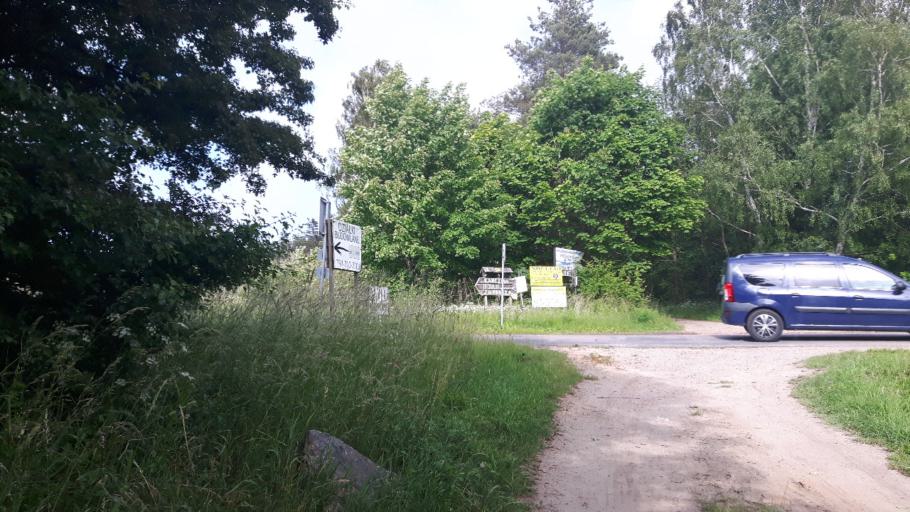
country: PL
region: Pomeranian Voivodeship
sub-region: Slupsk
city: Slupsk
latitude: 54.6004
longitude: 17.0121
